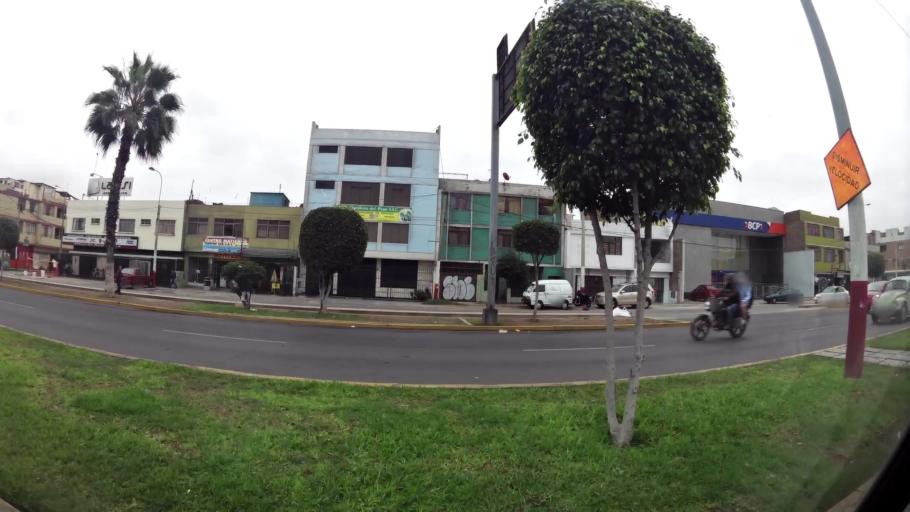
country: PE
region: Callao
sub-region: Callao
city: Callao
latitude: -12.0530
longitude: -77.0946
